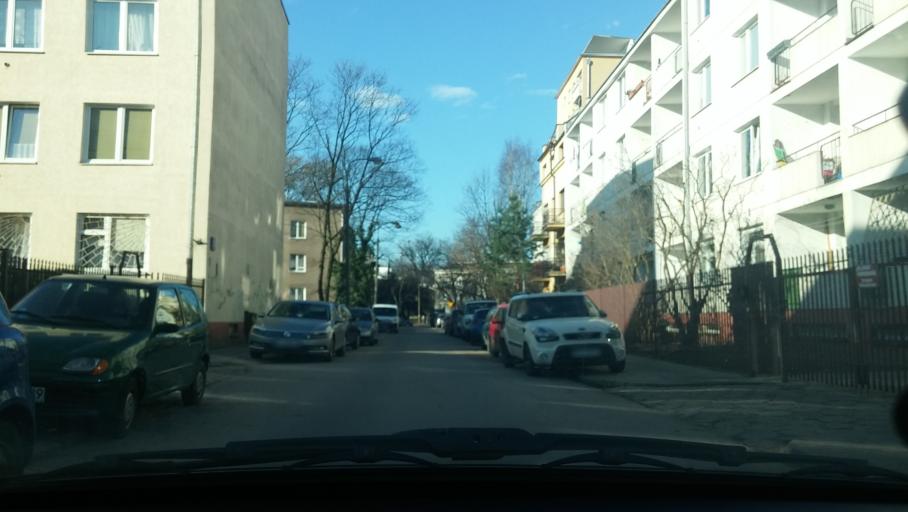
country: PL
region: Masovian Voivodeship
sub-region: Warszawa
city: Praga Polnoc
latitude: 52.2387
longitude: 21.0578
